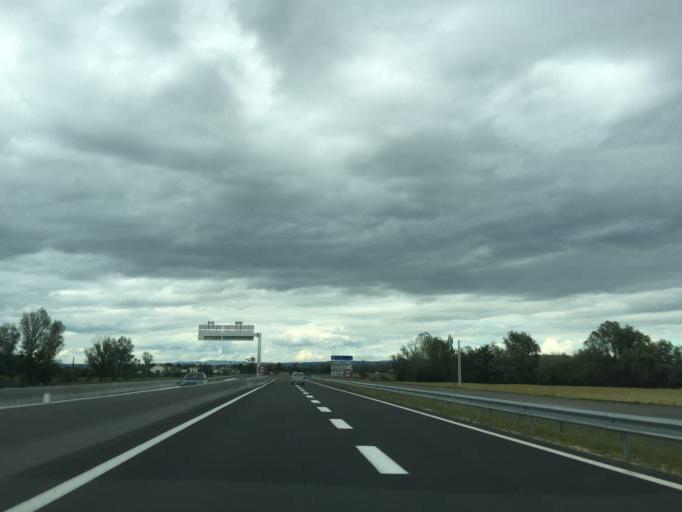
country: FR
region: Rhone-Alpes
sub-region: Departement de la Loire
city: Sury-le-Comtal
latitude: 45.5136
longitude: 4.1954
